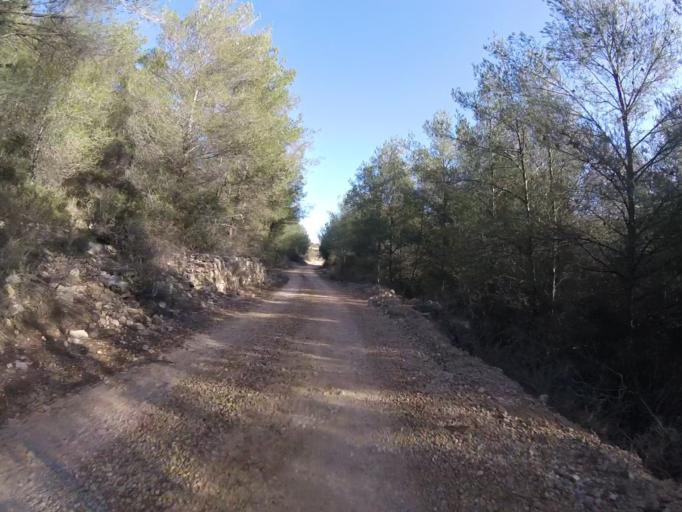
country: ES
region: Valencia
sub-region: Provincia de Castello
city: Torreblanca
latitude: 40.2535
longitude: 0.1891
